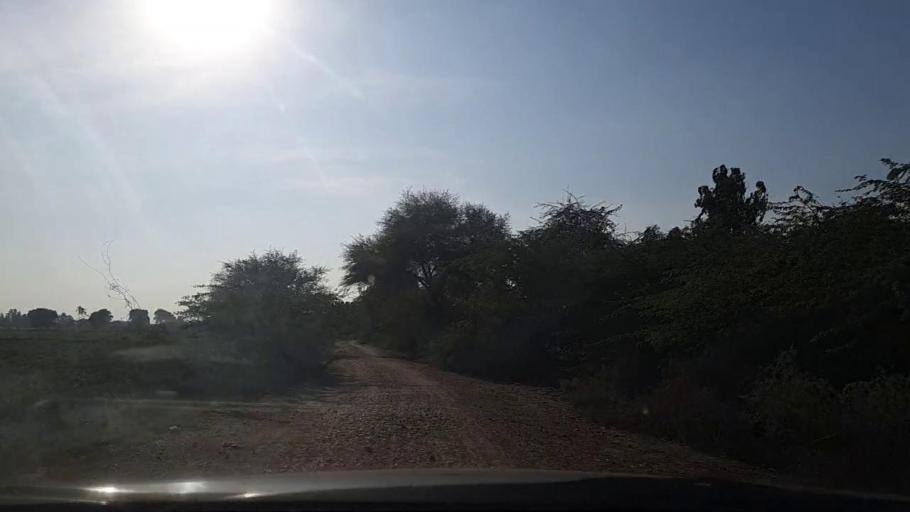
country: PK
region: Sindh
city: Mirpur Sakro
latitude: 24.5349
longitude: 67.6369
